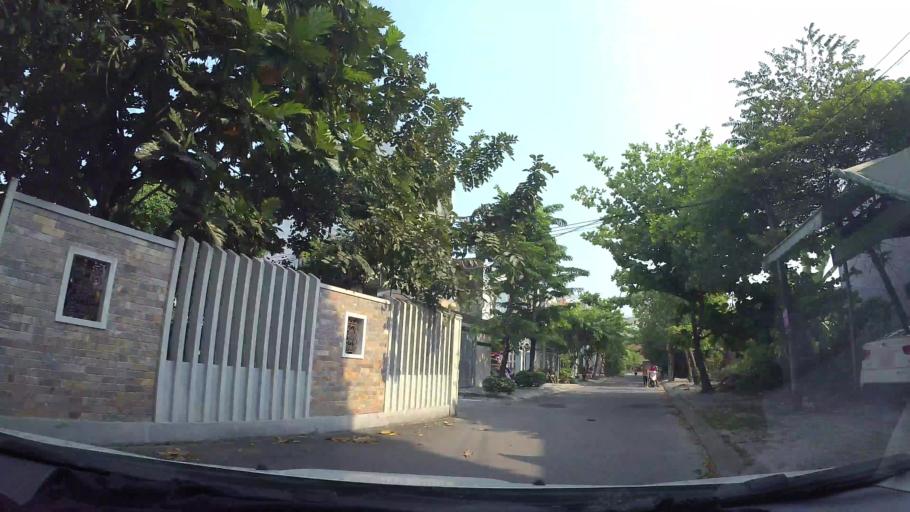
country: VN
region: Da Nang
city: Cam Le
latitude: 16.0175
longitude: 108.2015
